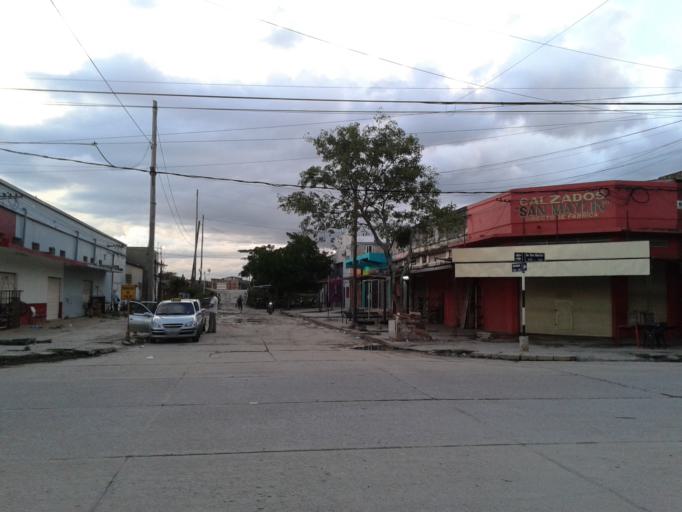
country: AR
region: Formosa
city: Clorinda
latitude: -25.2872
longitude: -57.7103
